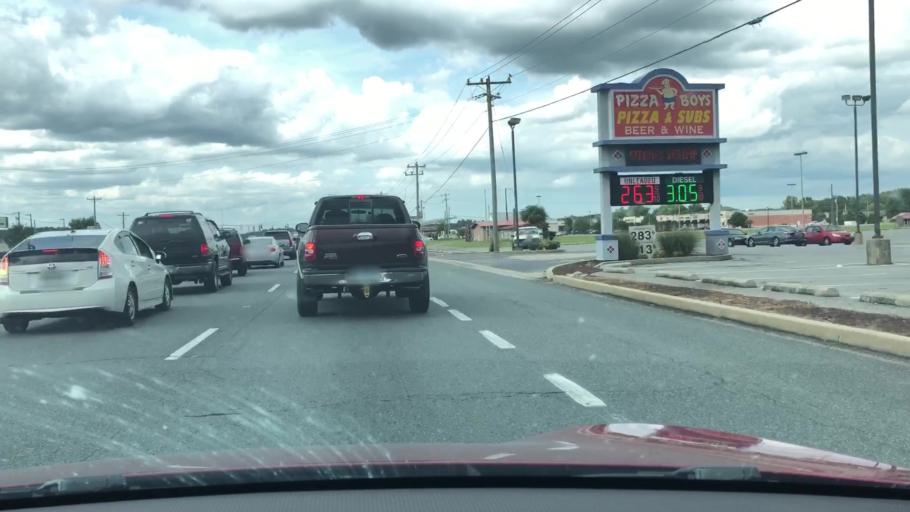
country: US
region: Delaware
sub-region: Sussex County
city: Delmar
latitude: 38.4535
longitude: -75.5586
